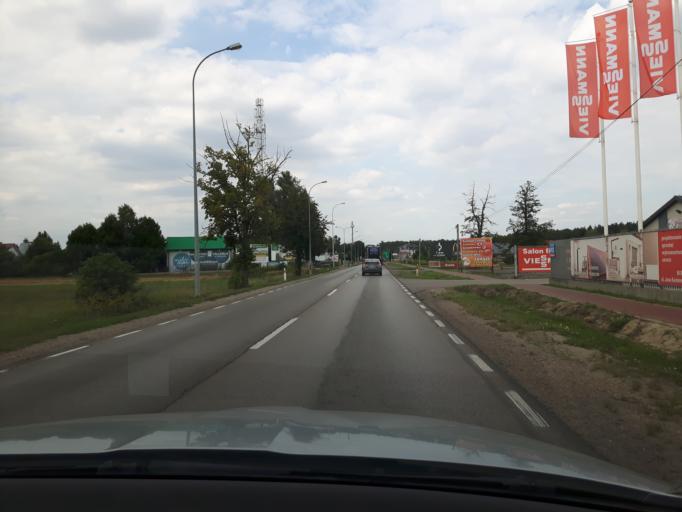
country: PL
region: Masovian Voivodeship
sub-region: Powiat legionowski
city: Stanislawow Pierwszy
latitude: 52.3747
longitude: 21.0291
